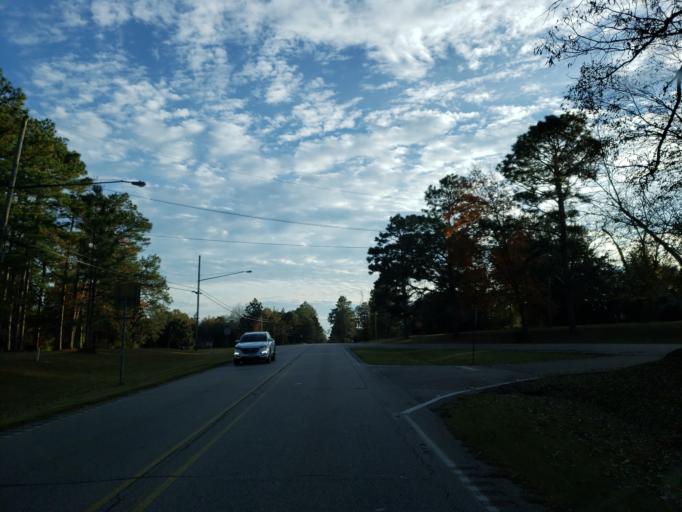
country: US
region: Mississippi
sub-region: Lamar County
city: Purvis
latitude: 31.1260
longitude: -89.4075
